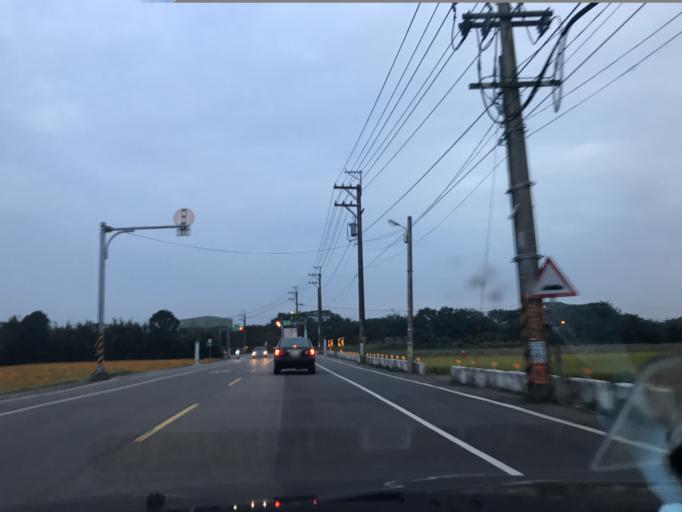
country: TW
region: Taiwan
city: Daxi
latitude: 24.9157
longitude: 121.2312
